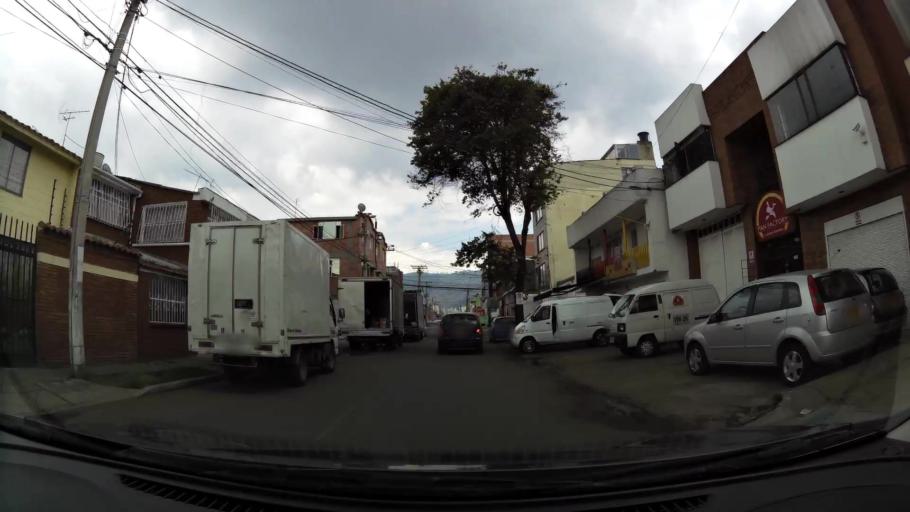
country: CO
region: Bogota D.C.
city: Barrio San Luis
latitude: 4.7416
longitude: -74.0437
